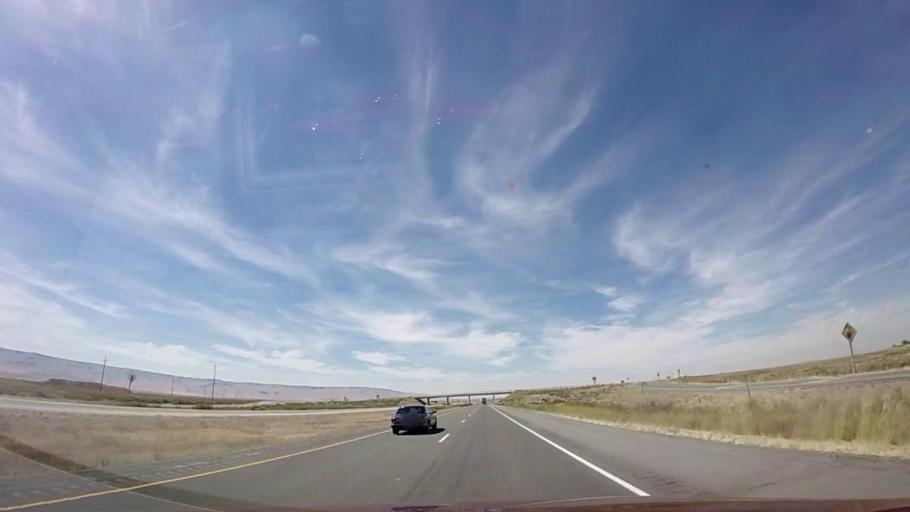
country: US
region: Idaho
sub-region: Minidoka County
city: Rupert
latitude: 42.4134
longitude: -113.3168
